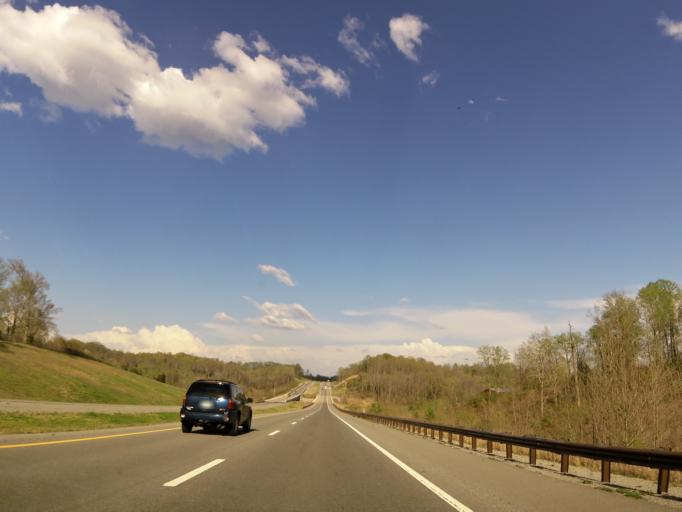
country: US
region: Tennessee
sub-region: Williamson County
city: Thompson's Station
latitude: 35.8161
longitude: -87.0252
